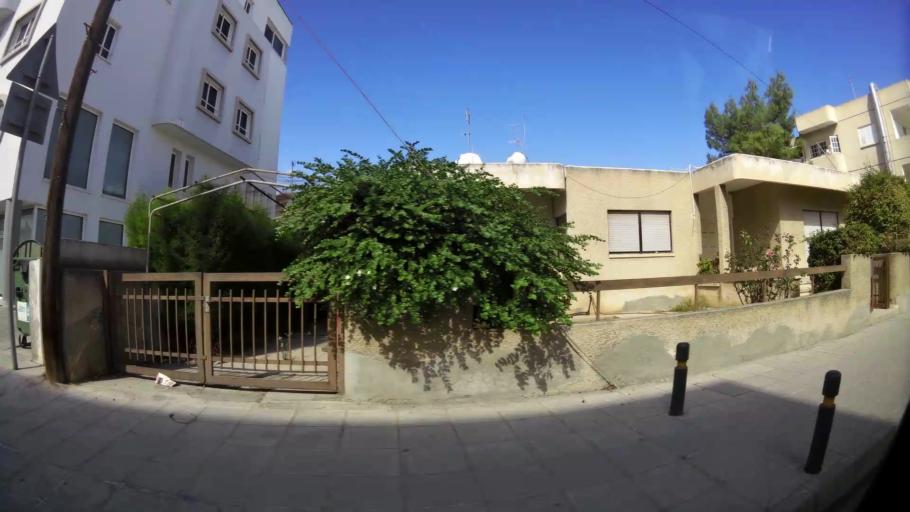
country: CY
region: Lefkosia
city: Nicosia
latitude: 35.1404
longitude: 33.3685
